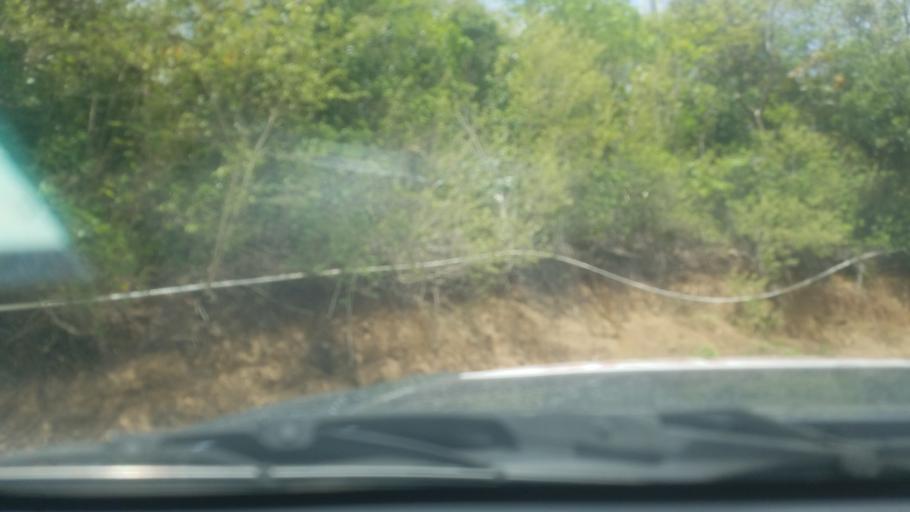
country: LC
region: Laborie Quarter
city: Laborie
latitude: 13.7491
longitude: -60.9888
